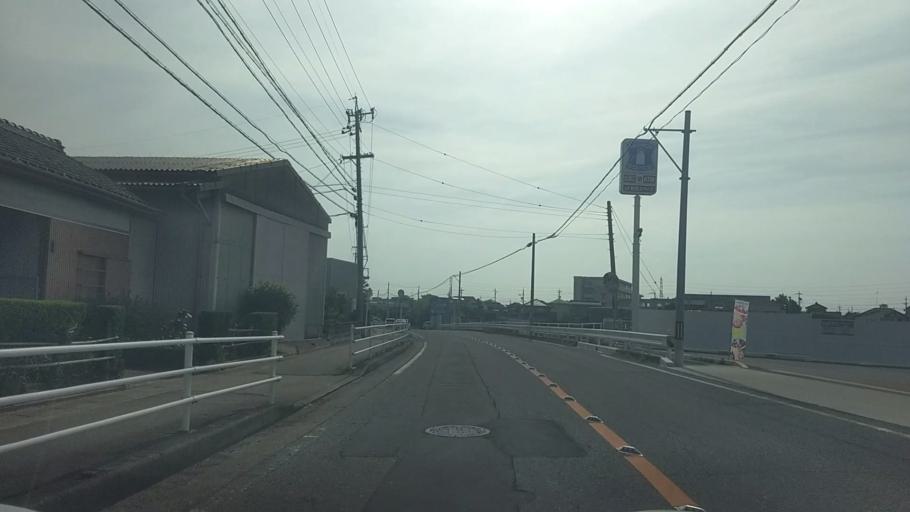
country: JP
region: Aichi
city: Anjo
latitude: 34.9578
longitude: 137.1037
